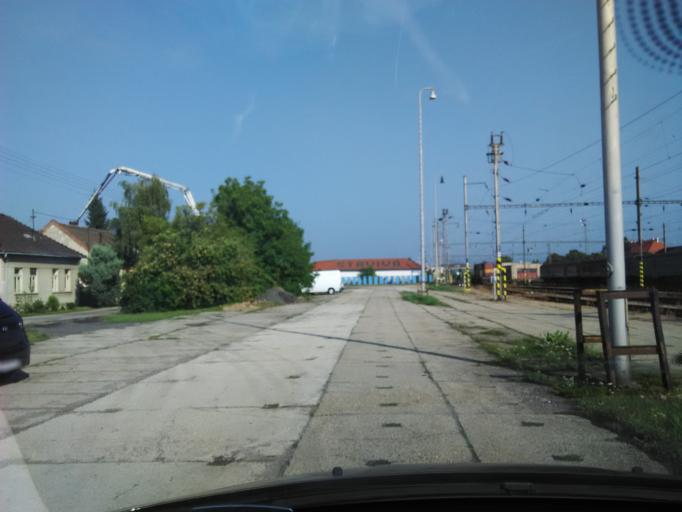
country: SK
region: Nitriansky
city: Levice
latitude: 48.2106
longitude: 18.5925
